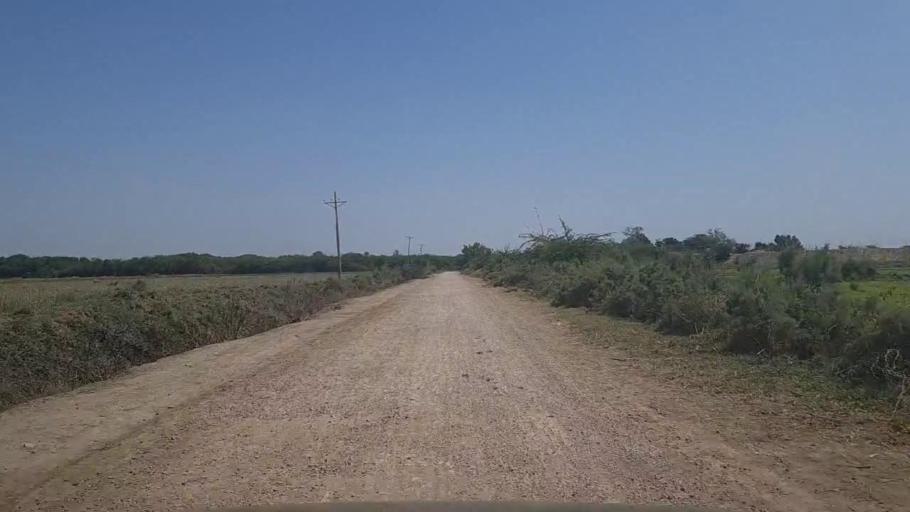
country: PK
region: Sindh
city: Thatta
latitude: 24.7867
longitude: 68.0054
